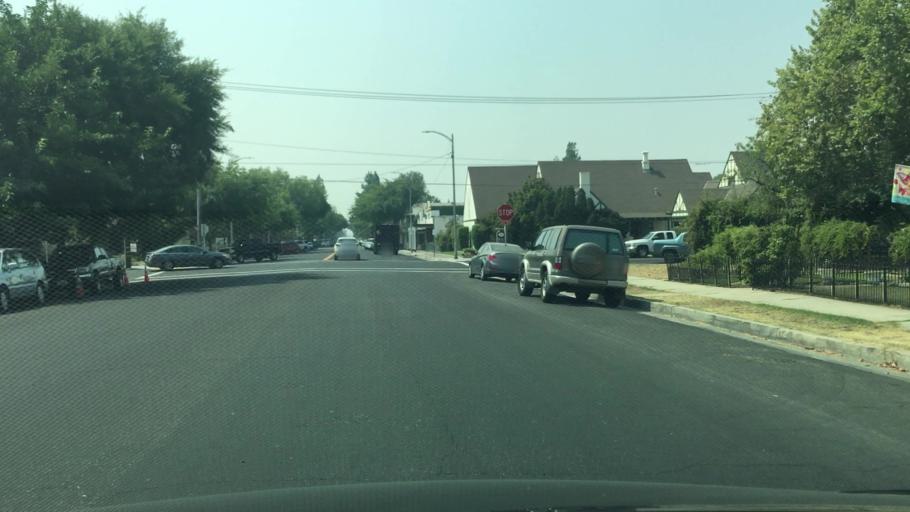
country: US
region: California
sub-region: Fresno County
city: Clovis
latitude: 36.8271
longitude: -119.7021
